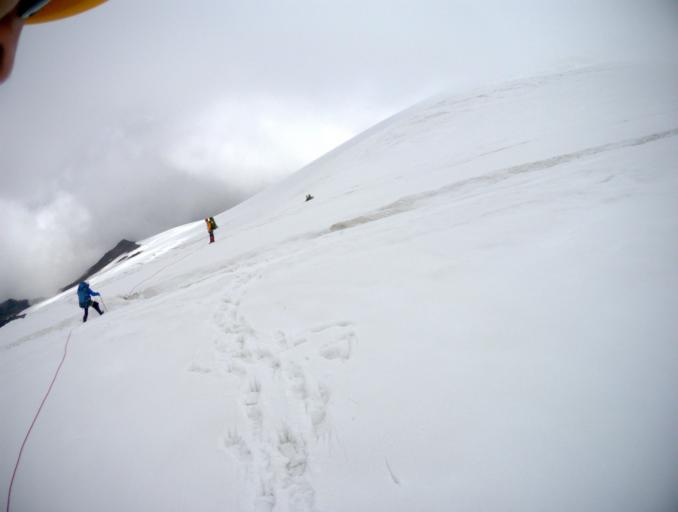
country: RU
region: Kabardino-Balkariya
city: Terskol
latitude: 43.3809
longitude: 42.4644
